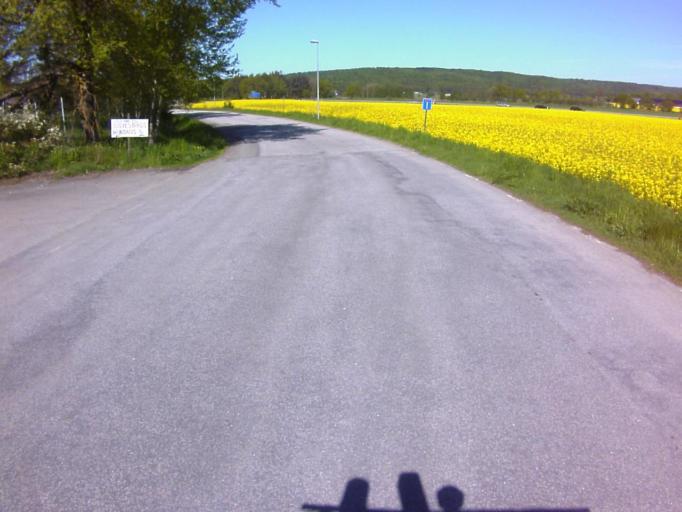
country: SE
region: Blekinge
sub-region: Solvesborgs Kommun
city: Soelvesborg
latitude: 56.0668
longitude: 14.6315
